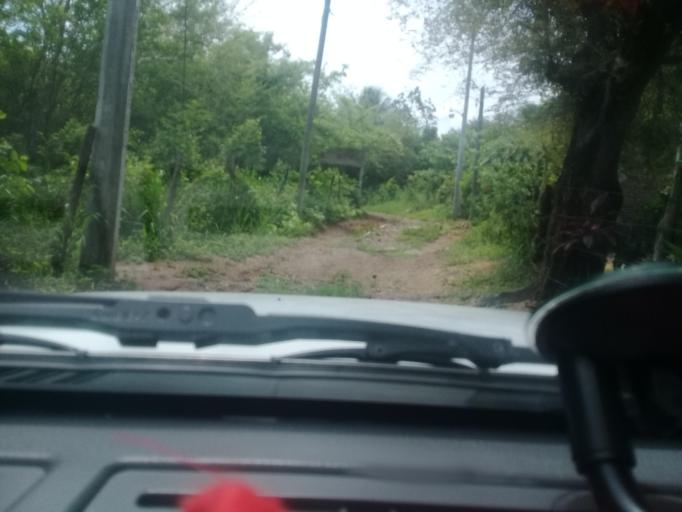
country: MX
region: Veracruz
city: Paso de Ovejas
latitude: 19.2828
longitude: -96.4330
